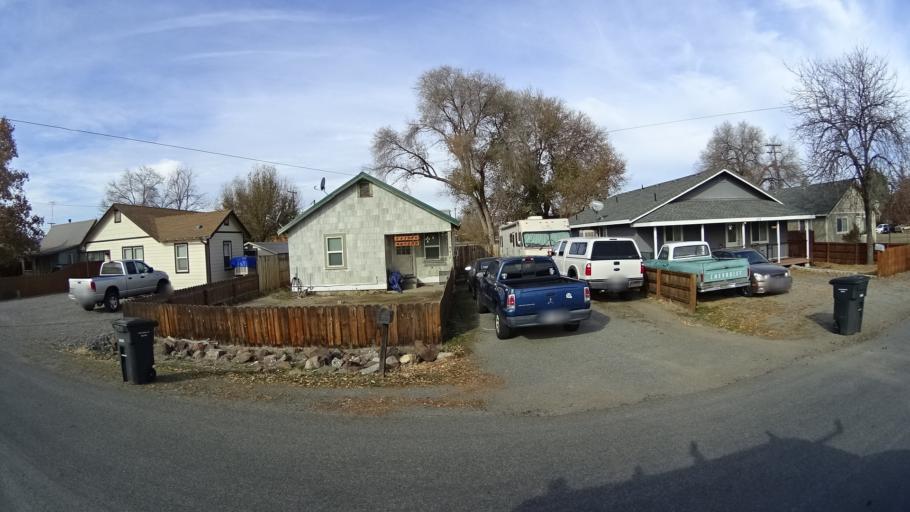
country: US
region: California
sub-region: Siskiyou County
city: Montague
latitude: 41.7231
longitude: -122.5273
